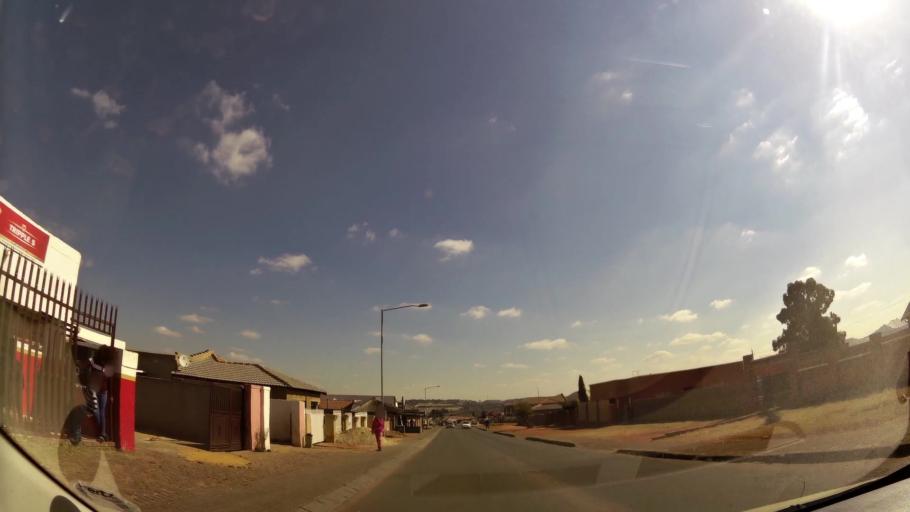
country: ZA
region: Gauteng
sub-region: West Rand District Municipality
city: Krugersdorp
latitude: -26.1493
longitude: 27.7737
